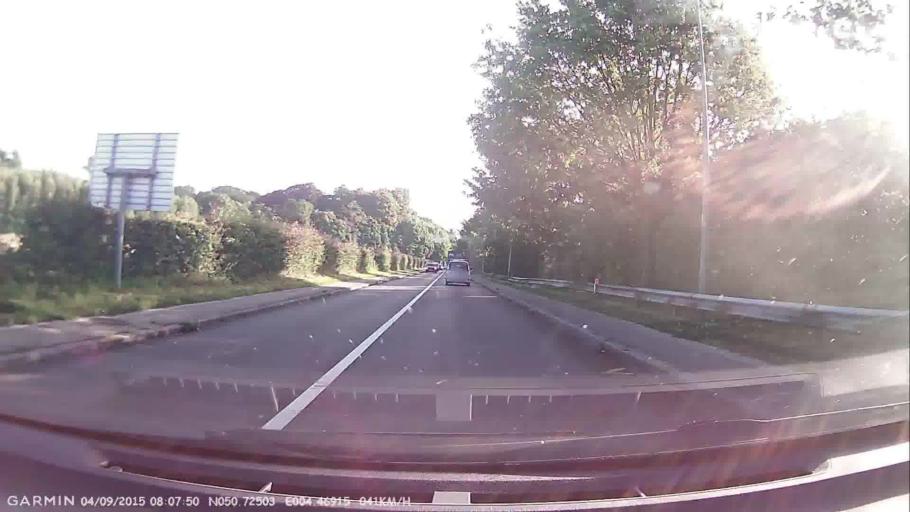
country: BE
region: Wallonia
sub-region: Province du Brabant Wallon
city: La Hulpe
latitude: 50.7251
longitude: 4.4692
